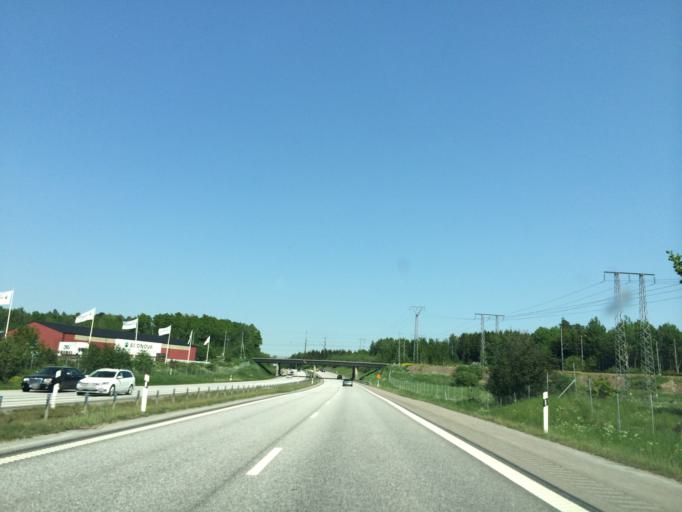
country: SE
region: OEstergoetland
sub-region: Norrkopings Kommun
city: Jursla
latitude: 58.6504
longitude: 16.1796
